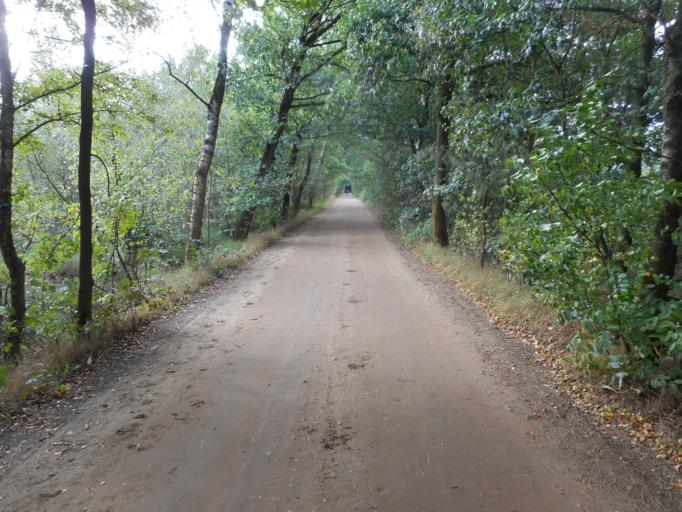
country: BE
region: Flanders
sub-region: Provincie Antwerpen
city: Lille
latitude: 51.2855
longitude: 4.8192
